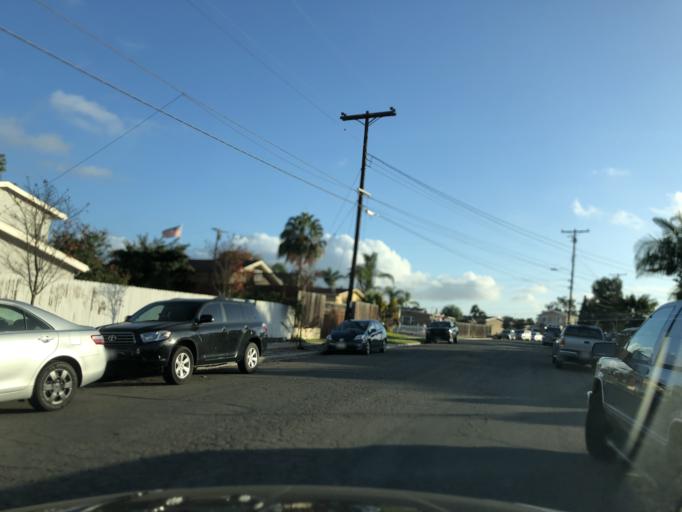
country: US
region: California
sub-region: San Diego County
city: San Diego
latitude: 32.8170
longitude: -117.1747
